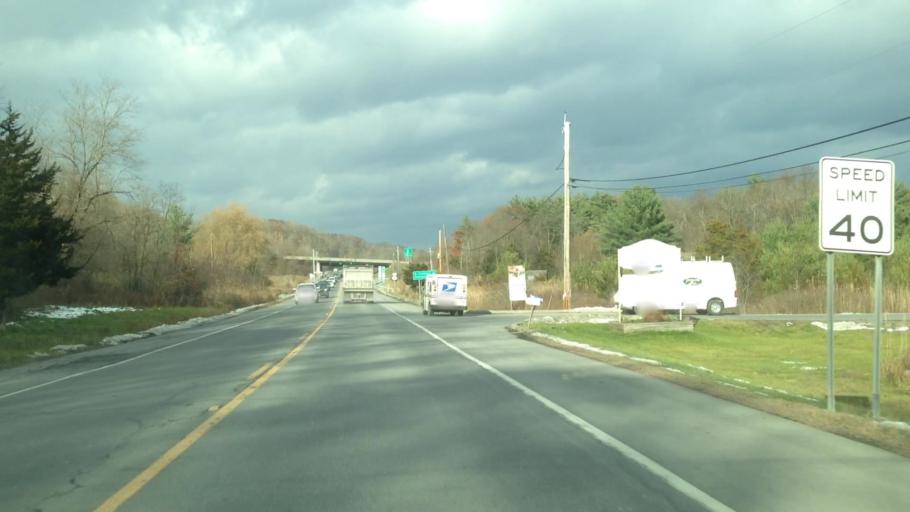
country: US
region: New York
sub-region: Ulster County
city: Lake Katrine
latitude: 41.9742
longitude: -73.9711
